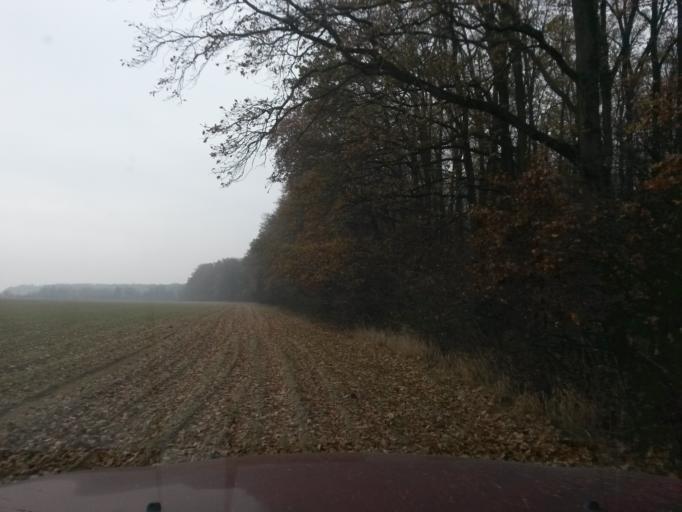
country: SK
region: Presovsky
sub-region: Okres Presov
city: Presov
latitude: 48.8908
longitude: 21.2816
